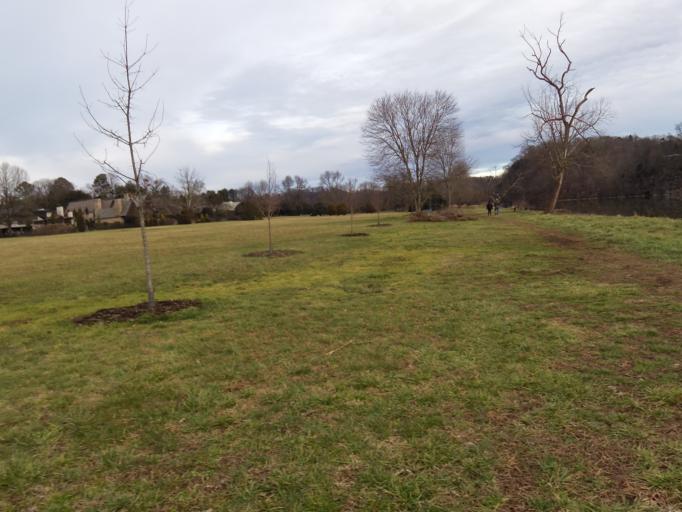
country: US
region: Tennessee
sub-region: Knox County
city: Knoxville
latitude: 35.9259
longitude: -83.9672
